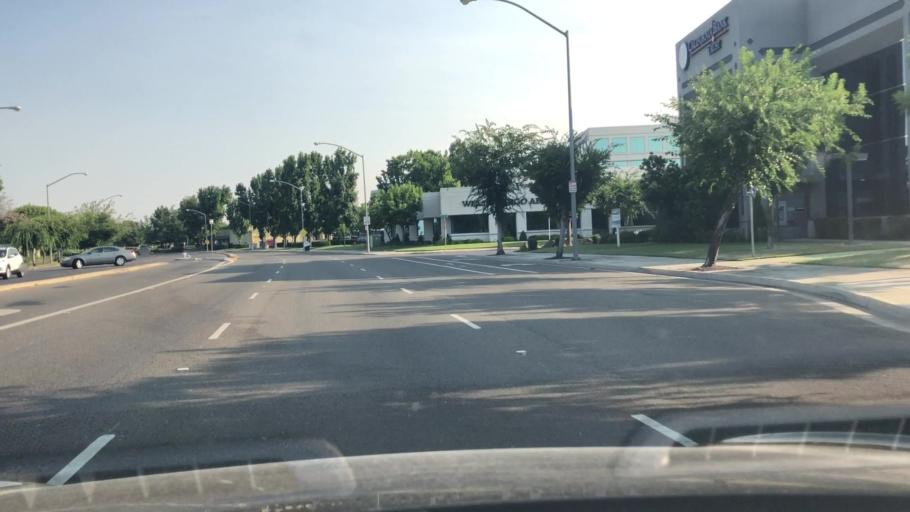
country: US
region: California
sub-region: Fresno County
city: Clovis
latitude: 36.8386
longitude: -119.7812
